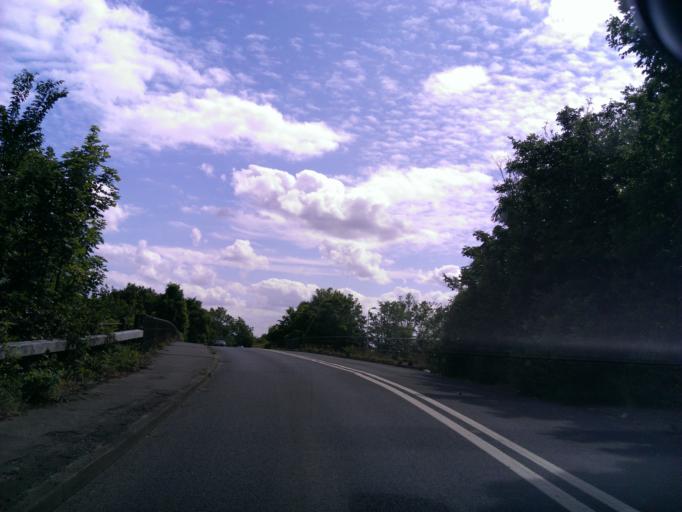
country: GB
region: England
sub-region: Essex
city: Hatfield Peverel
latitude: 51.7849
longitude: 0.6178
